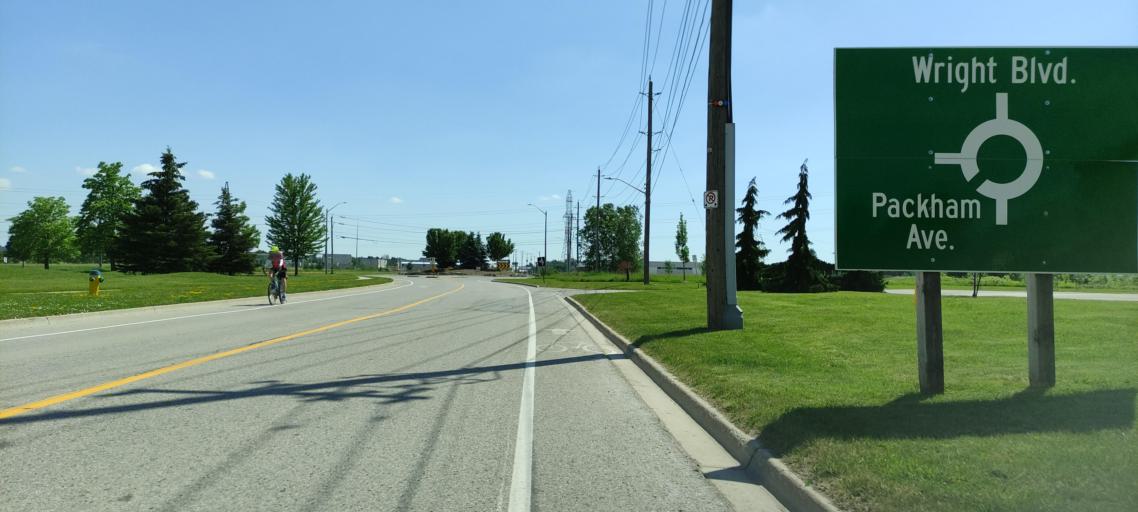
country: CA
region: Ontario
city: Stratford
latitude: 43.3538
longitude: -81.0125
